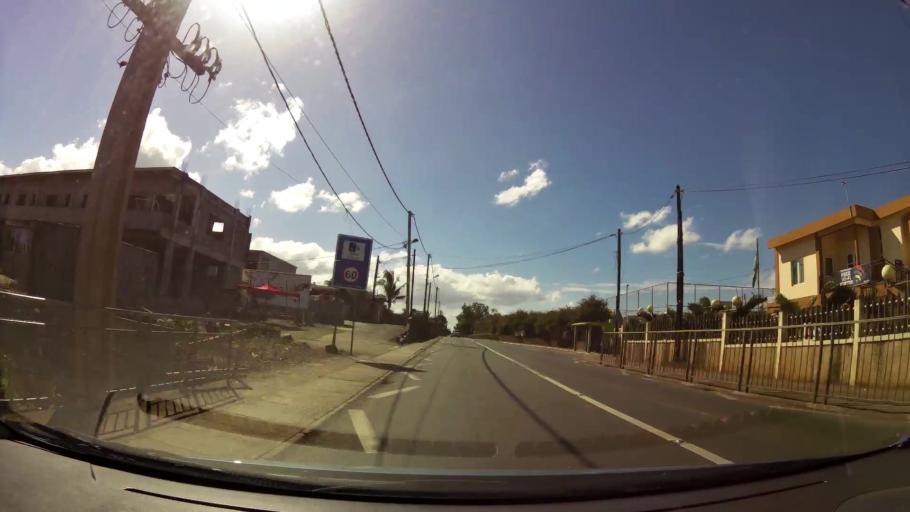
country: MU
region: Black River
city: Cascavelle
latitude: -20.2514
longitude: 57.4194
